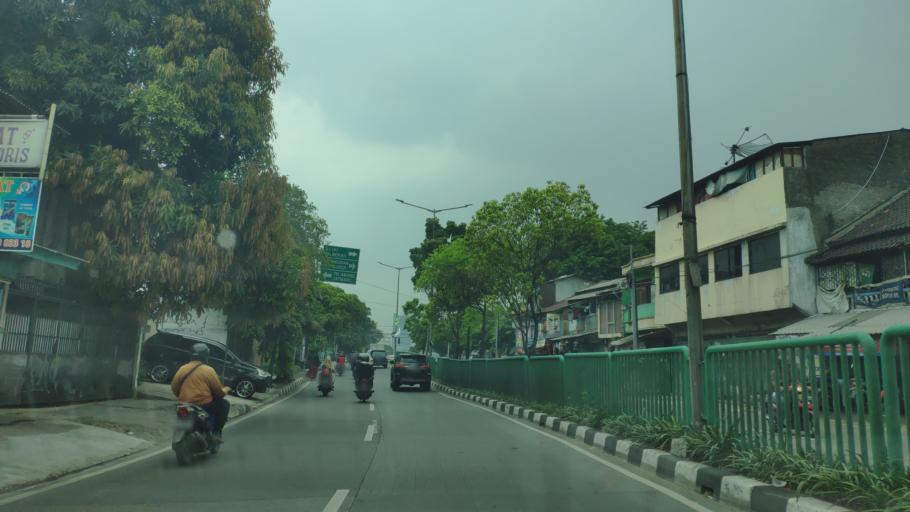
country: ID
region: Jakarta Raya
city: Jakarta
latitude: -6.1880
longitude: 106.8070
